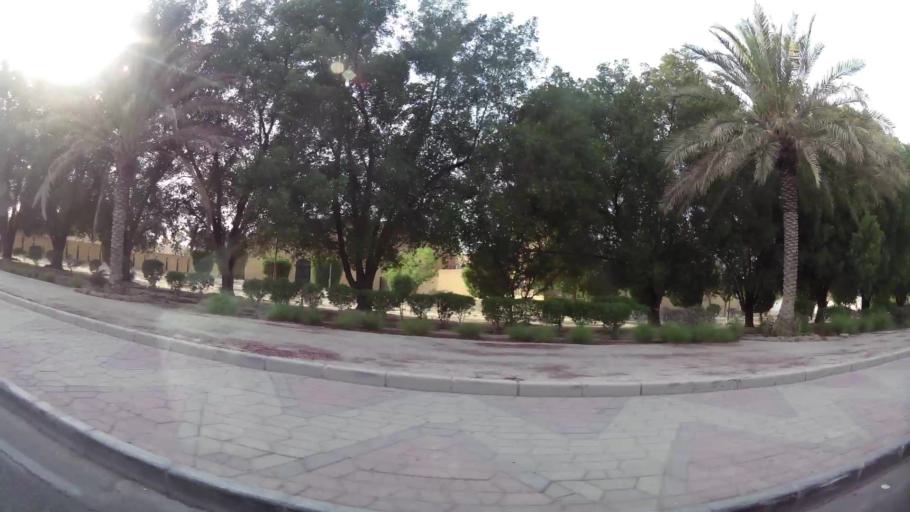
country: KW
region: Mubarak al Kabir
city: Sabah as Salim
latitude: 29.2588
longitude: 48.0551
